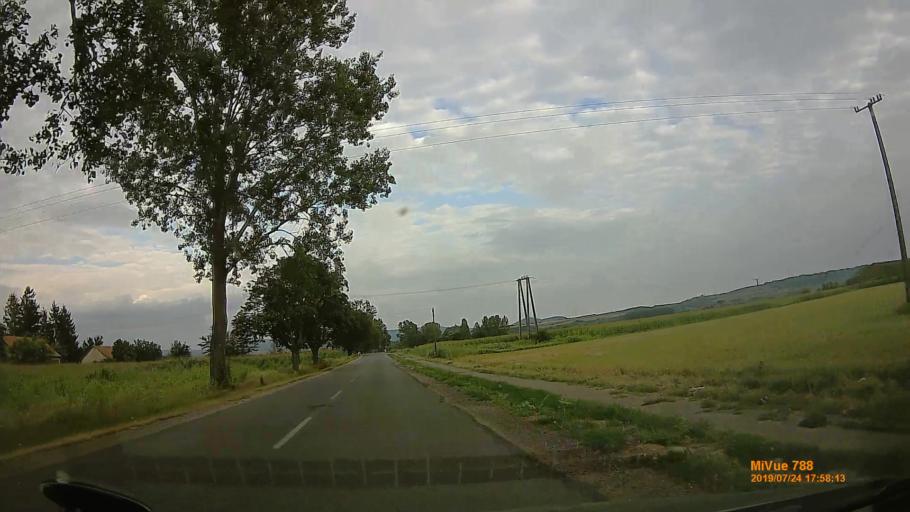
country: HU
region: Borsod-Abauj-Zemplen
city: Encs
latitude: 48.3264
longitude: 21.1448
